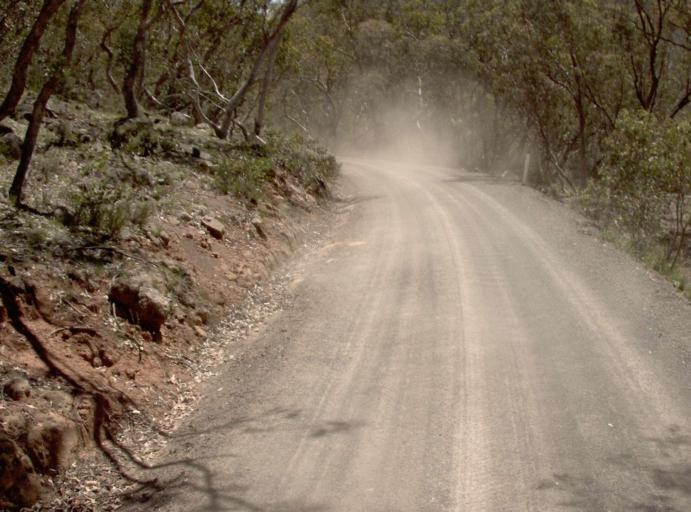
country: AU
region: New South Wales
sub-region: Snowy River
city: Jindabyne
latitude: -37.0744
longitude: 148.4706
